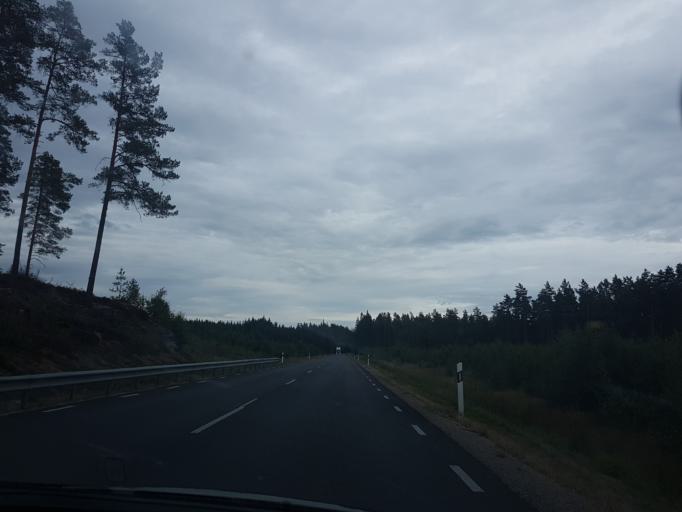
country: SE
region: Joenkoeping
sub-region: Vetlanda Kommun
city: Vetlanda
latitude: 57.3580
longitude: 15.1124
